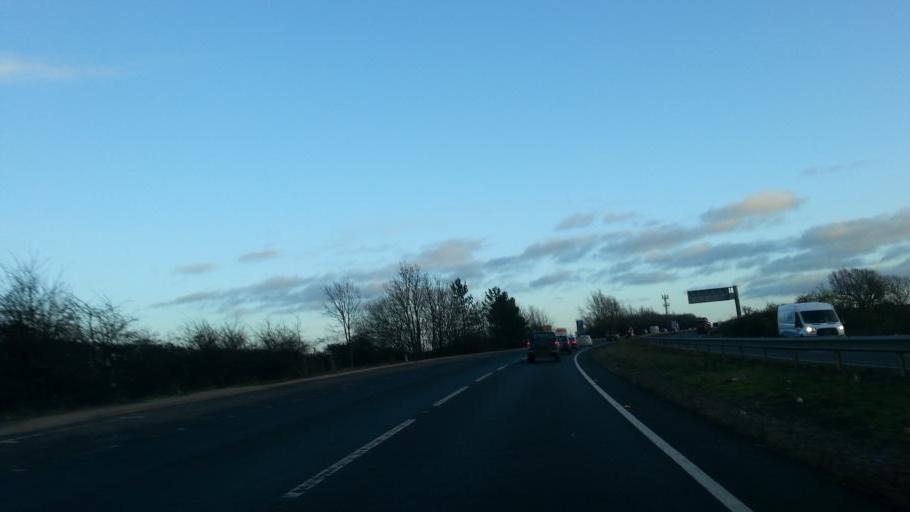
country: GB
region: England
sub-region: Northamptonshire
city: Thrapston
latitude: 52.3844
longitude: -0.4908
